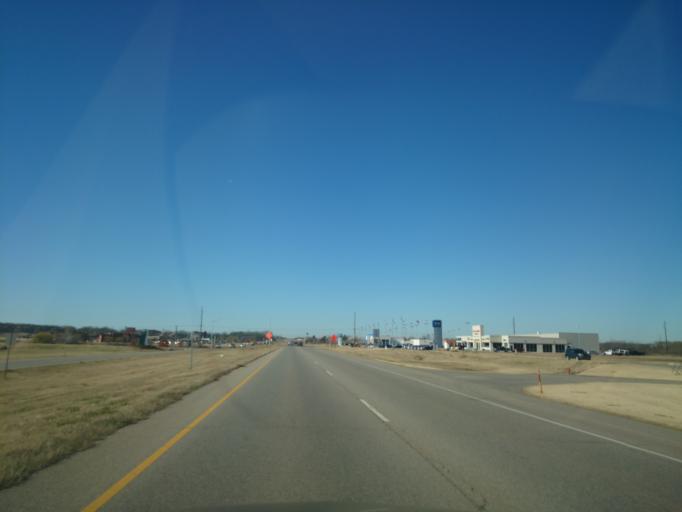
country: US
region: Oklahoma
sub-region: Payne County
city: Stillwater
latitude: 36.1162
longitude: -97.1104
